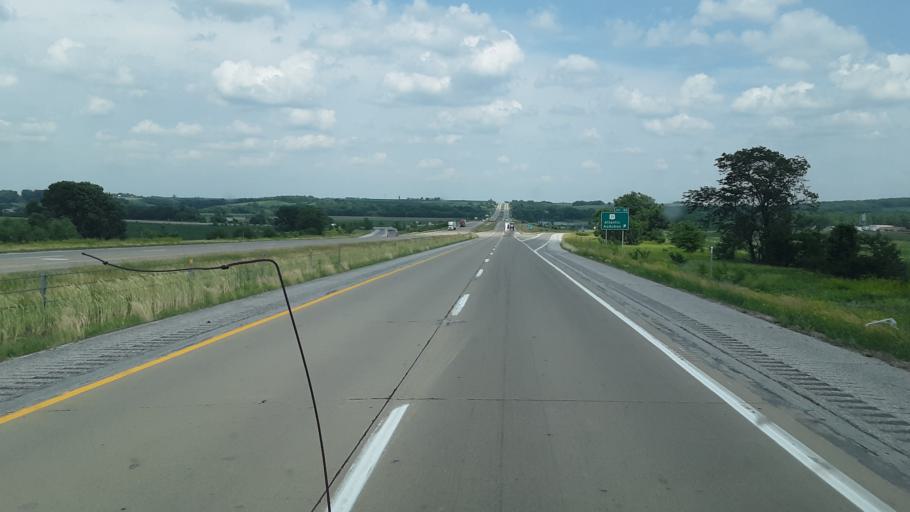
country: US
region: Iowa
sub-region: Cass County
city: Atlantic
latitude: 41.4972
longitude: -94.9534
